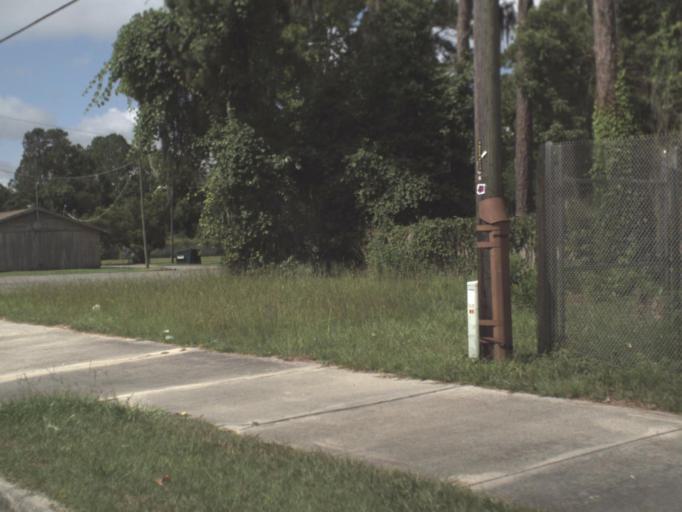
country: US
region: Florida
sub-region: Columbia County
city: Five Points
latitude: 30.2126
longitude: -82.6378
